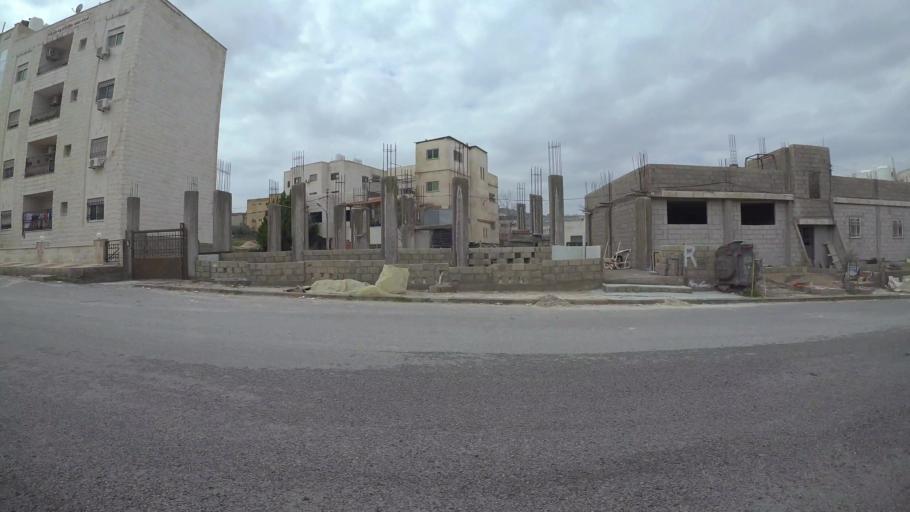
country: JO
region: Amman
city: Al Jubayhah
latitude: 32.0560
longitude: 35.8222
